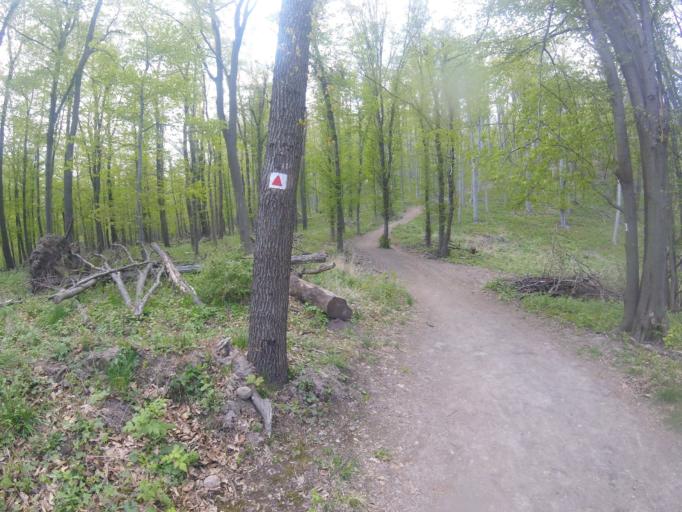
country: HU
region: Pest
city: Pilisszentkereszt
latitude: 47.7356
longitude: 18.9247
